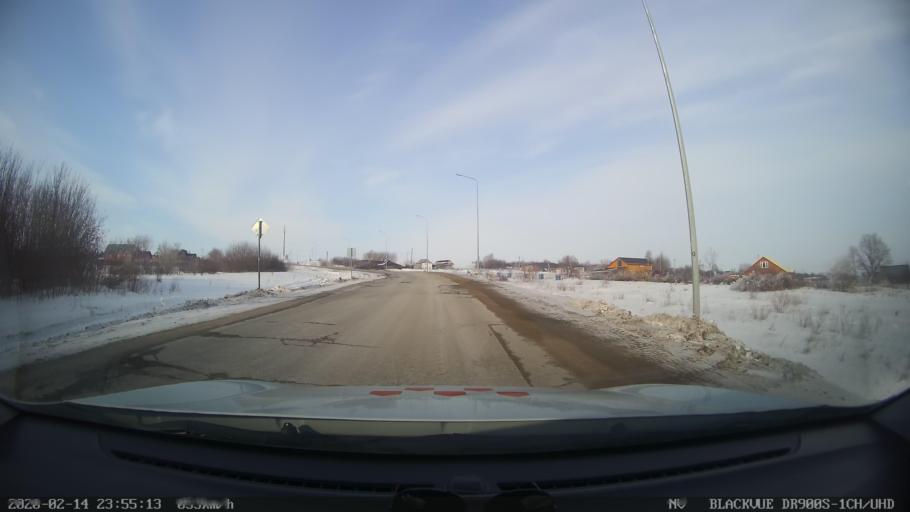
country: RU
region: Tatarstan
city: Kuybyshevskiy Zaton
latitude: 55.3151
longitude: 49.1445
